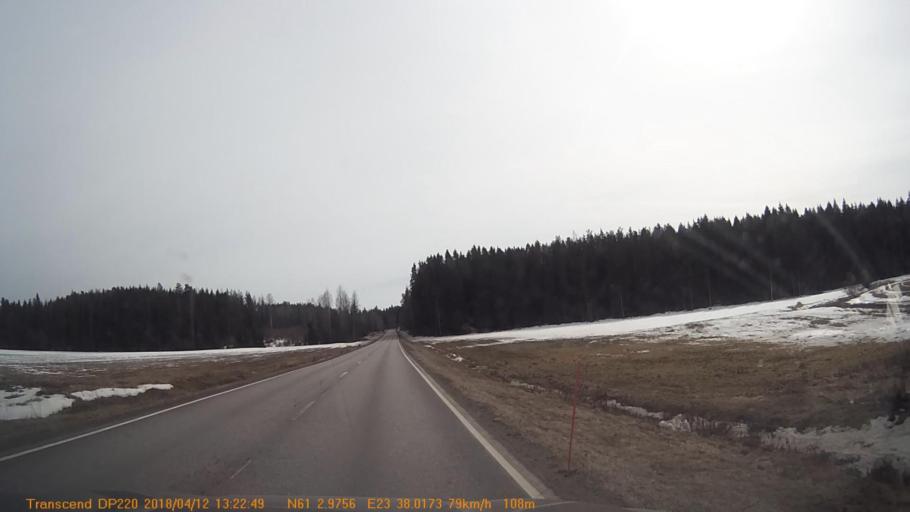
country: FI
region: Pirkanmaa
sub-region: Etelae-Pirkanmaa
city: Urjala
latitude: 61.0486
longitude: 23.6347
